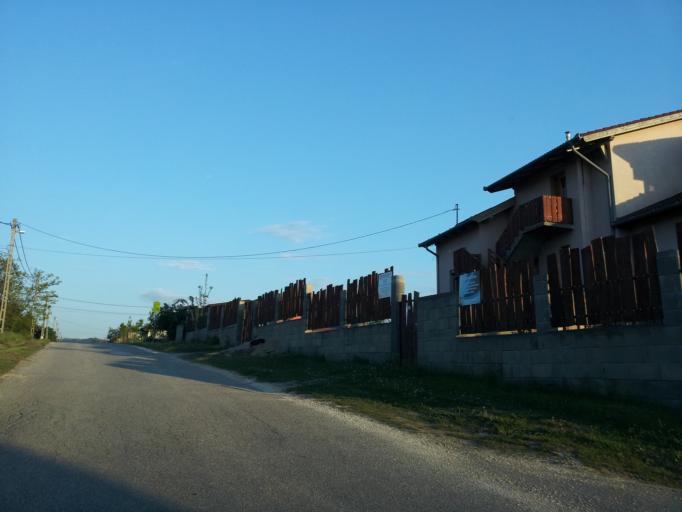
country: HU
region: Pest
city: Piliscsaba
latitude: 47.6245
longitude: 18.8133
